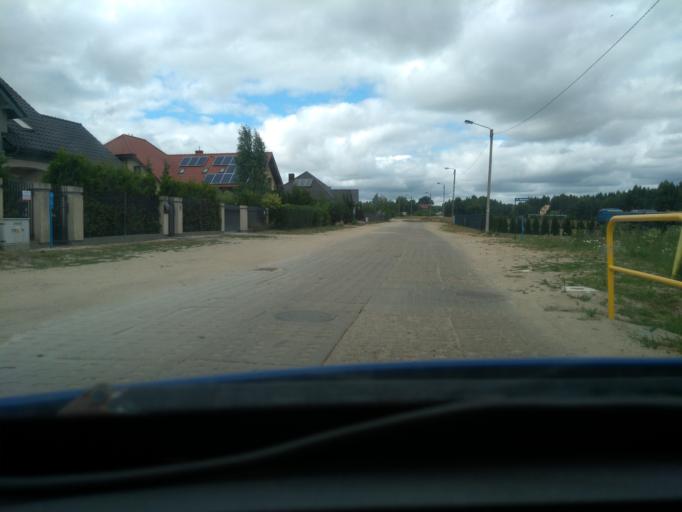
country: PL
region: Pomeranian Voivodeship
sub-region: Powiat kartuski
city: Banino
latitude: 54.3982
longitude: 18.3983
